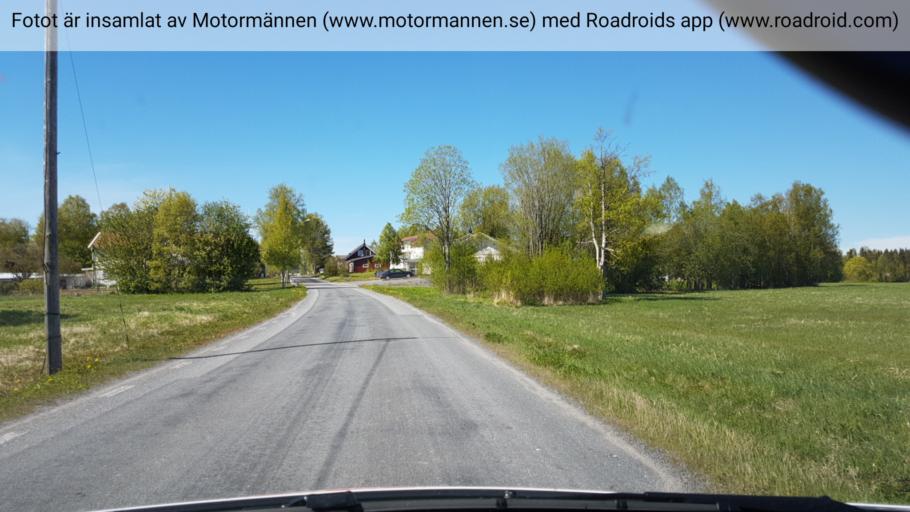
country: SE
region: Vaesternorrland
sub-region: OErnskoeldsviks Kommun
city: Husum
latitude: 63.2858
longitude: 19.0313
